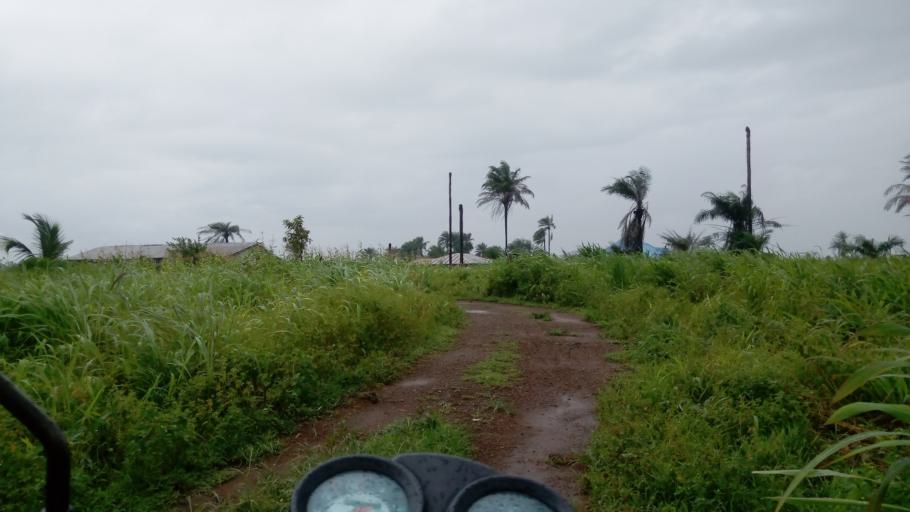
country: SL
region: Southern Province
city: Rotifunk
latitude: 8.4888
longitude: -12.7435
